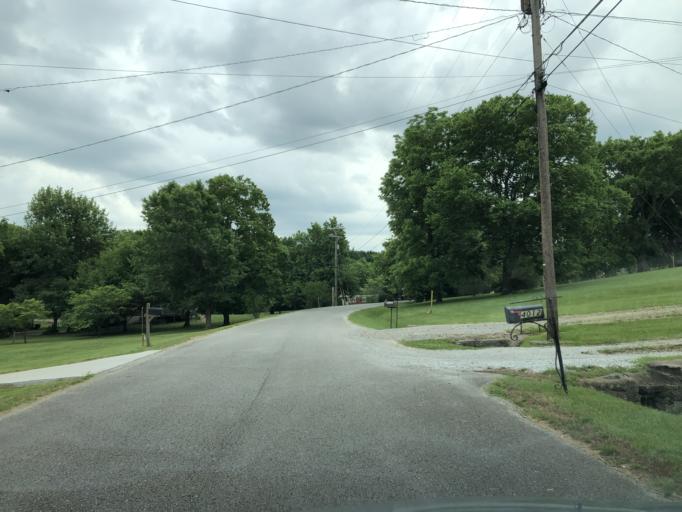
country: US
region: Tennessee
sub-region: Davidson County
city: Goodlettsville
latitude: 36.2677
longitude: -86.7653
